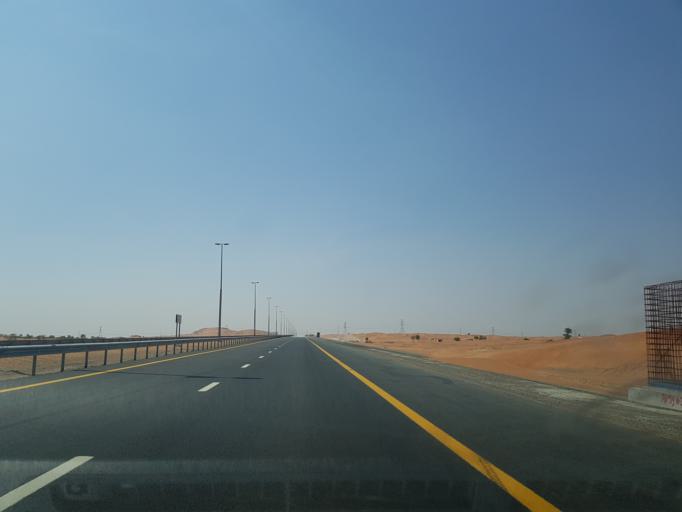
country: AE
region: Ash Shariqah
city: Adh Dhayd
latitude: 25.2434
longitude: 55.8659
